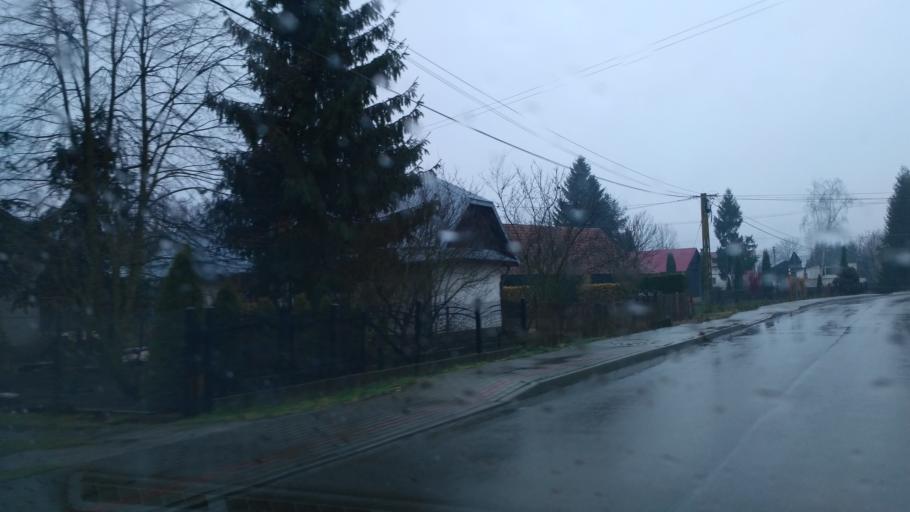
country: PL
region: Subcarpathian Voivodeship
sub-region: Powiat lancucki
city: Krzemienica
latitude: 50.0808
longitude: 22.1441
